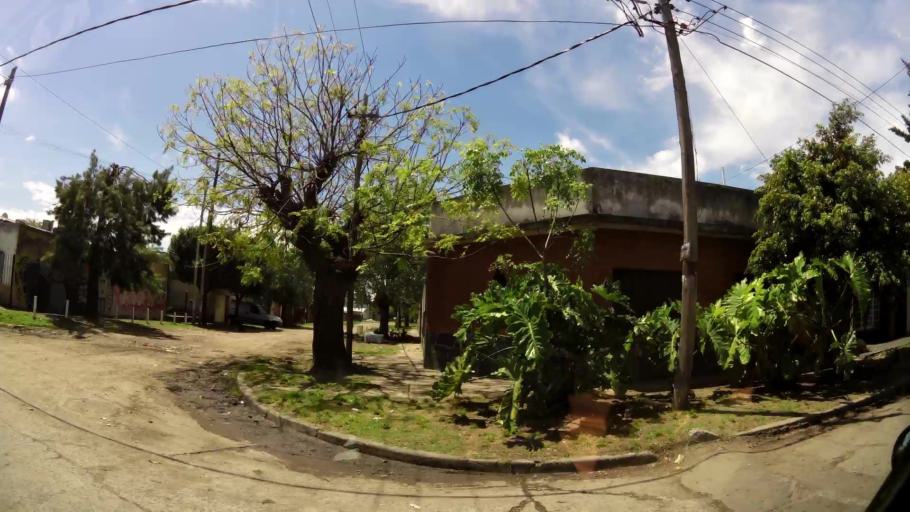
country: AR
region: Buenos Aires
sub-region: Partido de Quilmes
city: Quilmes
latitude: -34.7895
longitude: -58.2770
